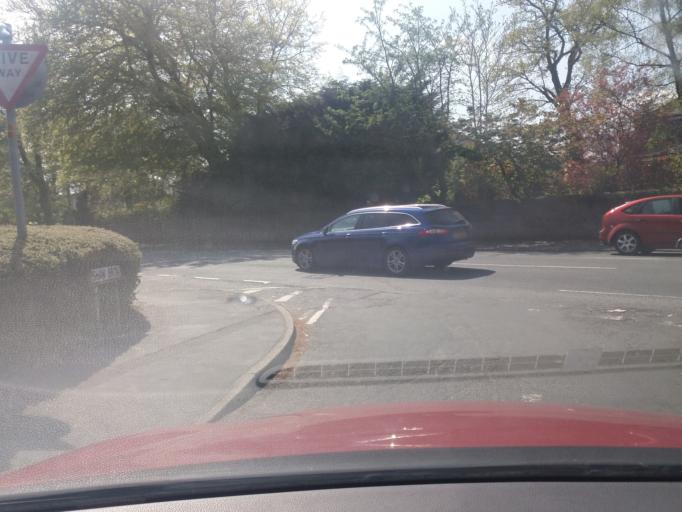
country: GB
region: England
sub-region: Lancashire
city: Clayton-le-Woods
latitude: 53.6831
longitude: -2.6383
